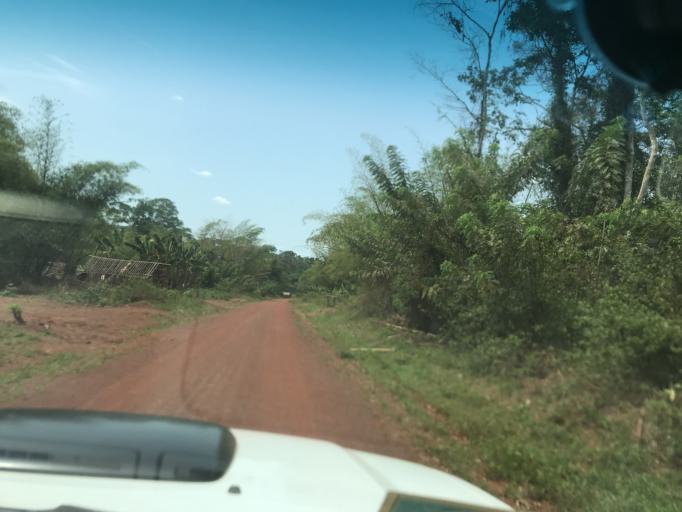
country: CD
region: Eastern Province
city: Buta
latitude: 2.2199
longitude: 25.2047
